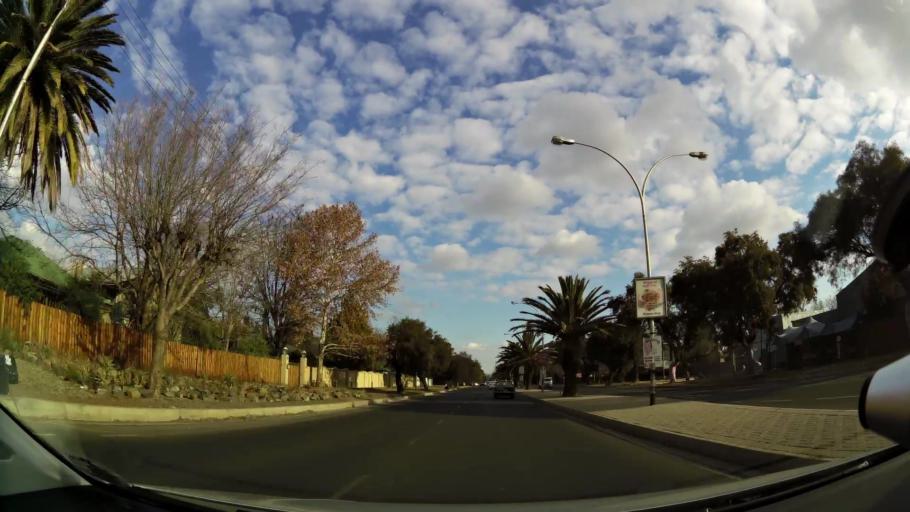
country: ZA
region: Orange Free State
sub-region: Mangaung Metropolitan Municipality
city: Bloemfontein
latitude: -29.1005
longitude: 26.2048
